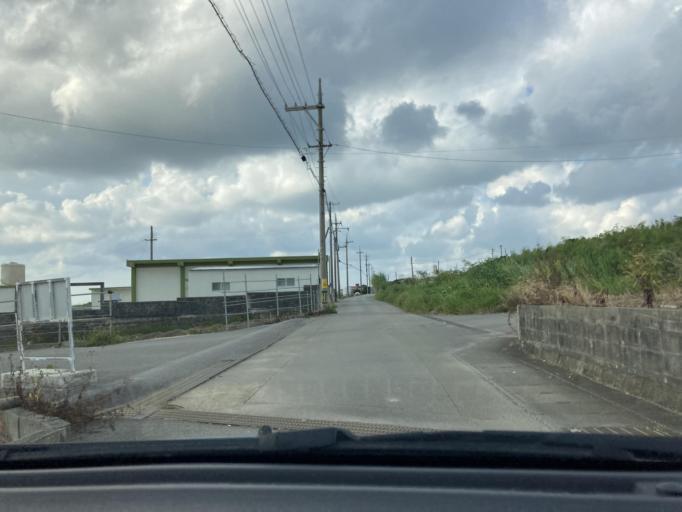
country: JP
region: Okinawa
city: Itoman
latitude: 26.0857
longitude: 127.6626
